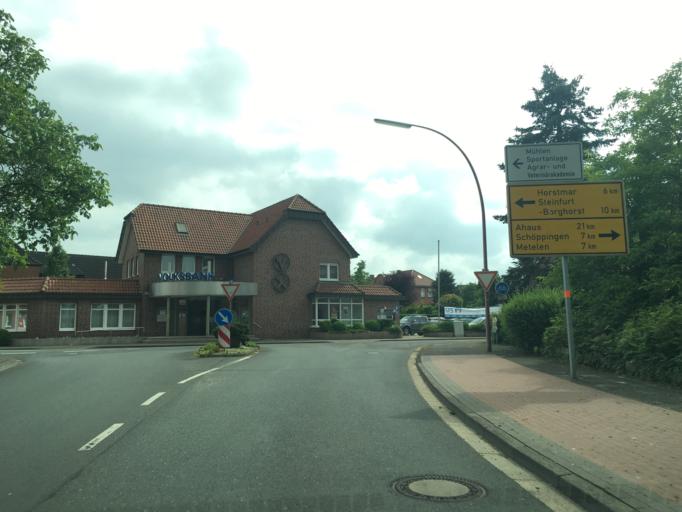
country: DE
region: North Rhine-Westphalia
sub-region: Regierungsbezirk Munster
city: Horstmar
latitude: 52.1144
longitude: 7.2935
